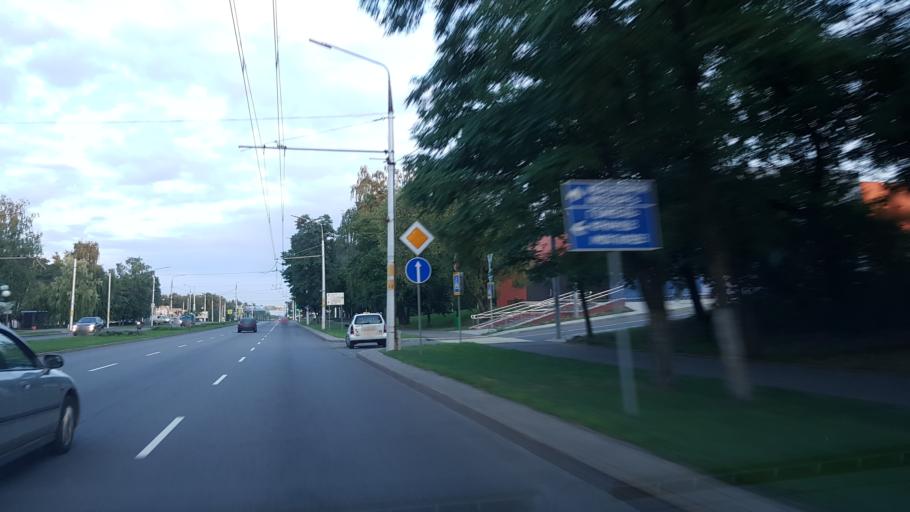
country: BY
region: Mogilev
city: Babruysk
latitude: 53.1802
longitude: 29.1958
